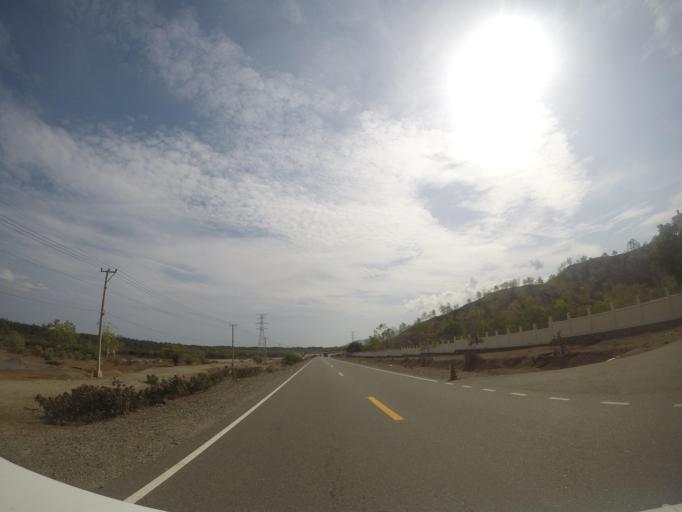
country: ID
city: Metinaro
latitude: -8.5131
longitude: 125.7831
